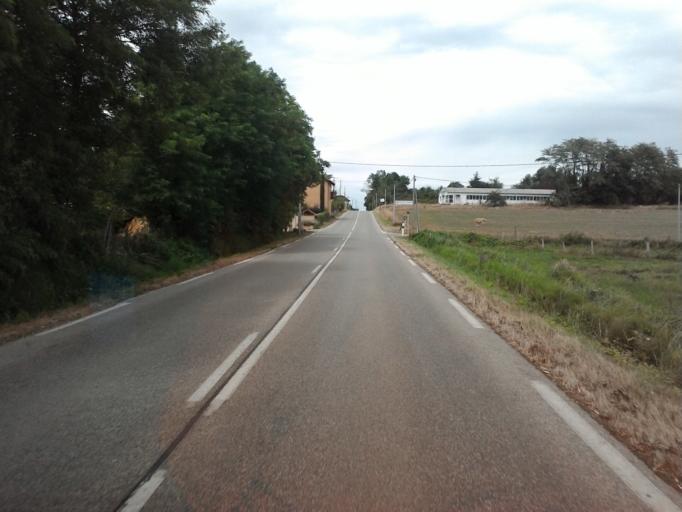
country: FR
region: Rhone-Alpes
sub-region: Departement de l'Isere
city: Morestel
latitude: 45.6611
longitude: 5.4782
